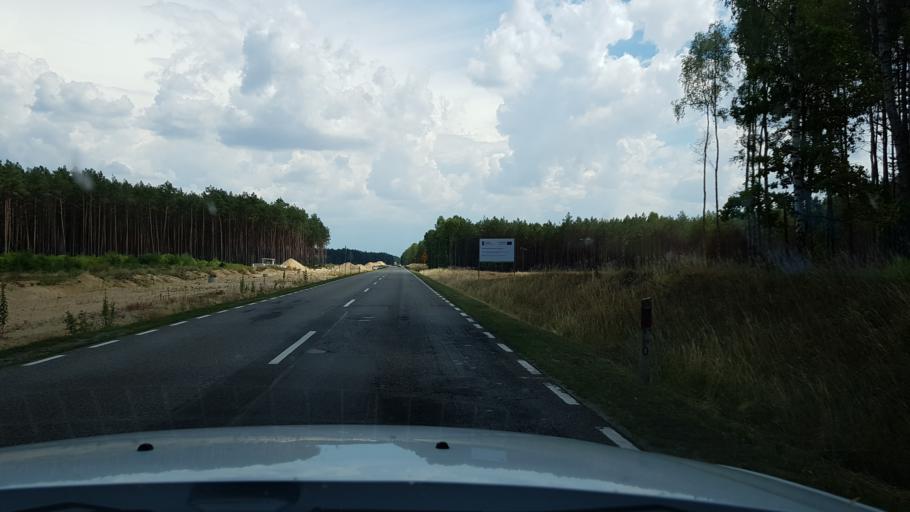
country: PL
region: West Pomeranian Voivodeship
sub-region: Powiat walecki
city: Walcz
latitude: 53.3005
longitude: 16.4133
